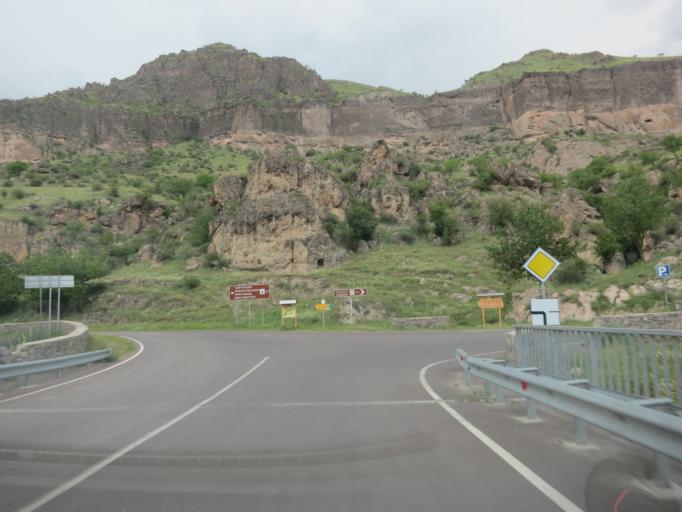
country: TR
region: Ardahan
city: Kurtkale
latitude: 41.3777
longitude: 43.2812
